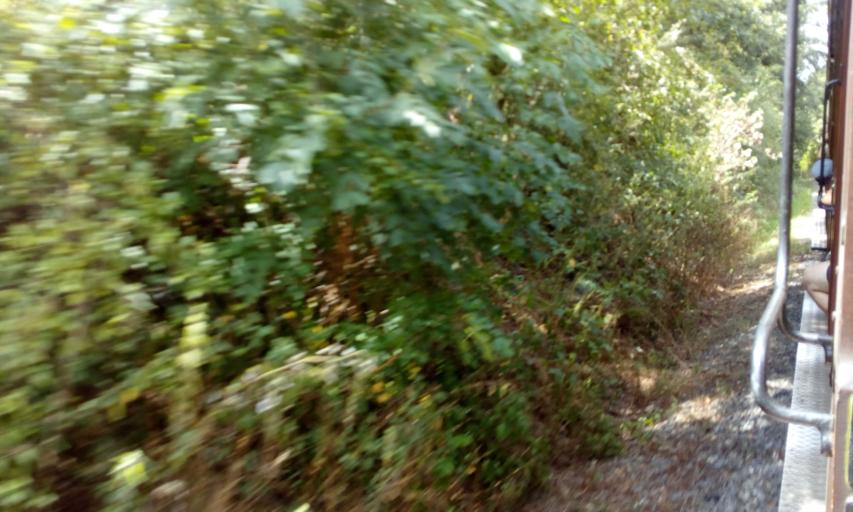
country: BE
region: Wallonia
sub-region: Province de Namur
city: Rochefort
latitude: 50.1256
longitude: 5.2053
